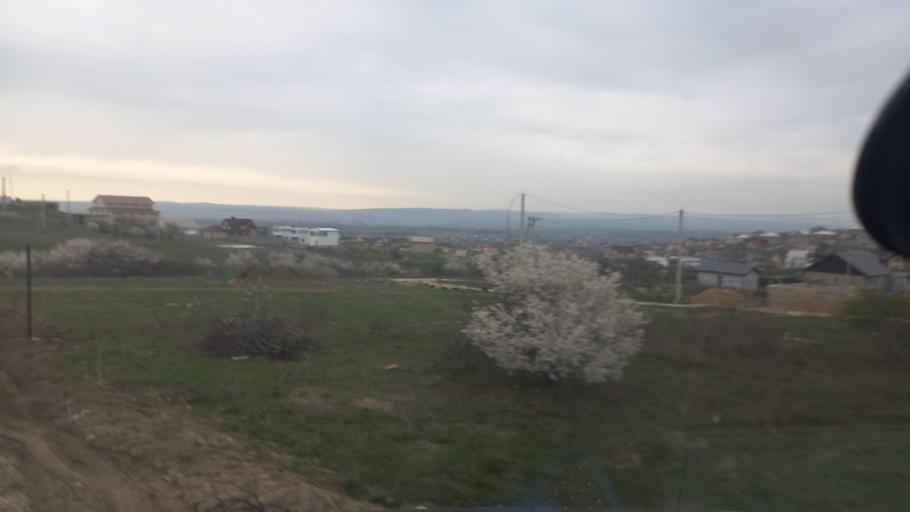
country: RU
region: Krasnodarskiy
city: Anapa
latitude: 44.8529
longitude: 37.3445
